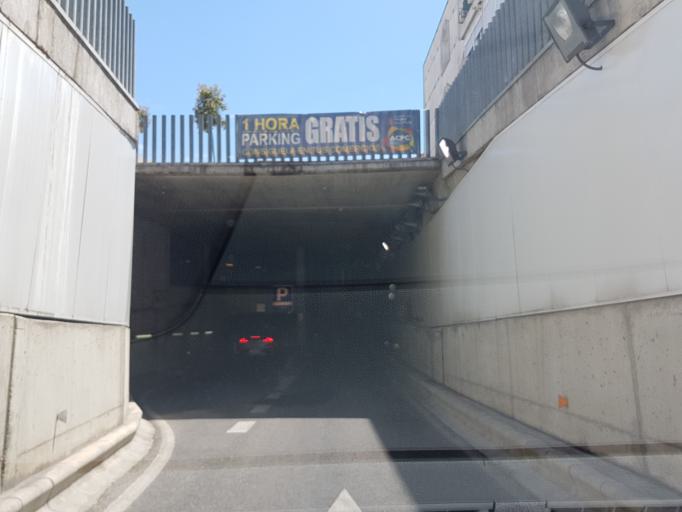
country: ES
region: Madrid
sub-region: Provincia de Madrid
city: Pozuelo de Alarcon
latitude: 40.4352
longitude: -3.8154
